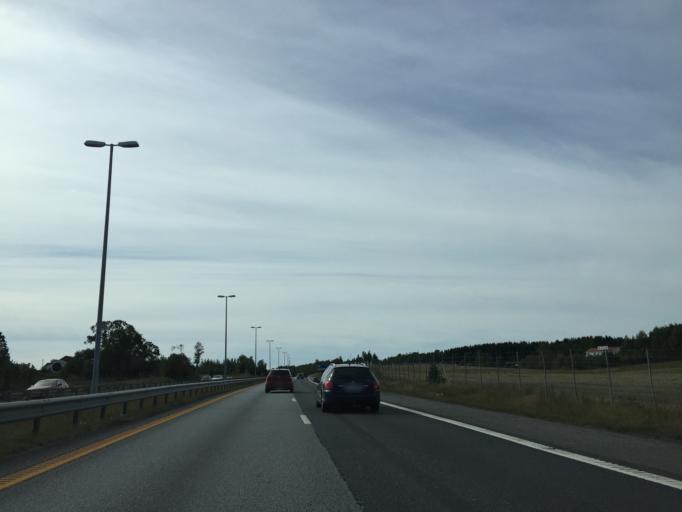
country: NO
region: Akershus
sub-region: Vestby
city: Vestby
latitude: 59.6316
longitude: 10.7373
